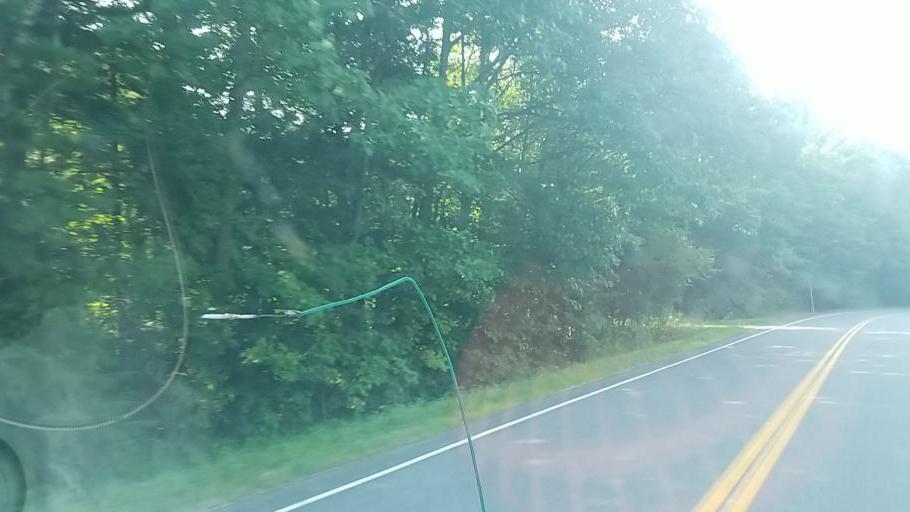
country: US
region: New York
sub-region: Fulton County
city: Gloversville
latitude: 43.1005
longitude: -74.3160
